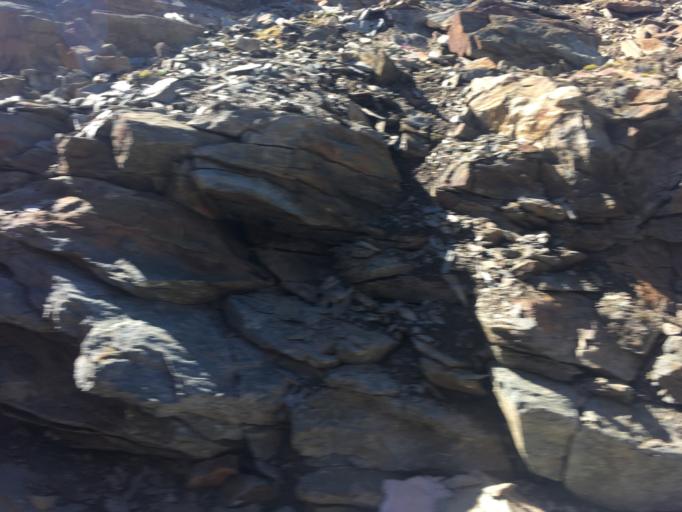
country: CH
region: Valais
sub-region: Visp District
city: Zermatt
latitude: 45.9850
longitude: 7.7748
